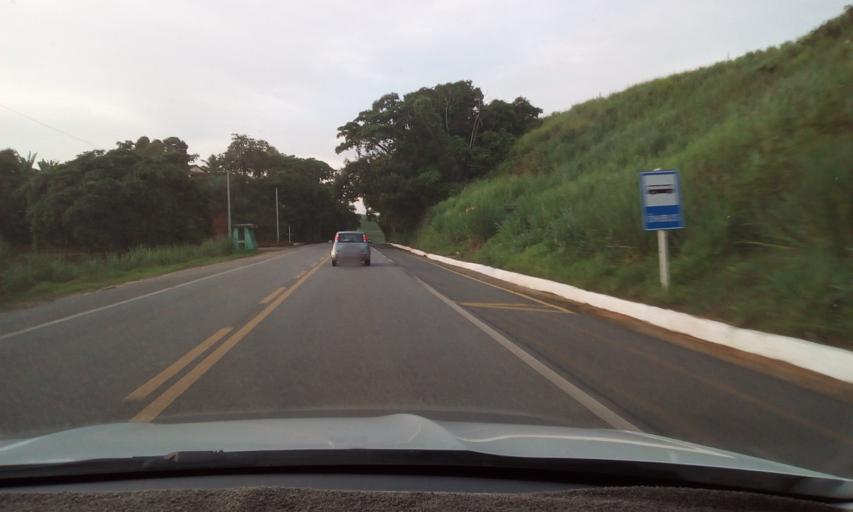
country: BR
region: Pernambuco
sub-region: Vicencia
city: Vicencia
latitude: -7.6444
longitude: -35.2539
